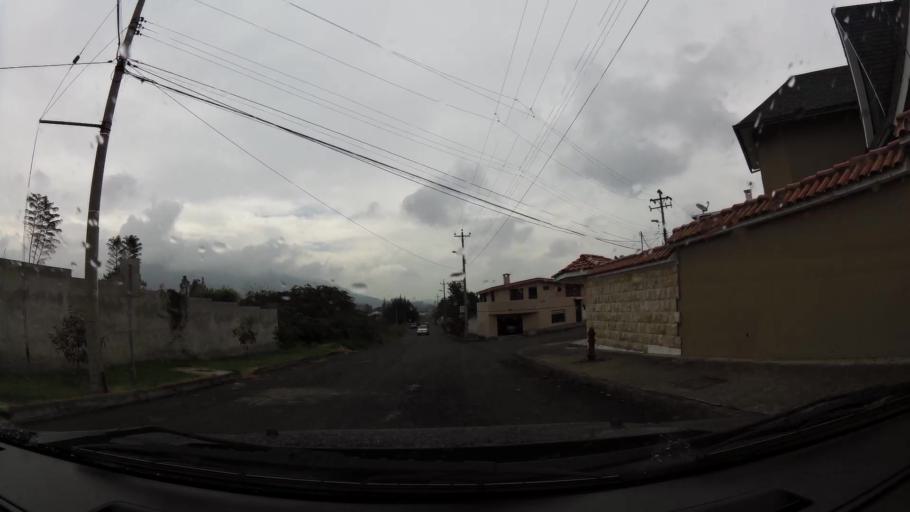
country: EC
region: Pichincha
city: Sangolqui
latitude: -0.2870
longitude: -78.4661
